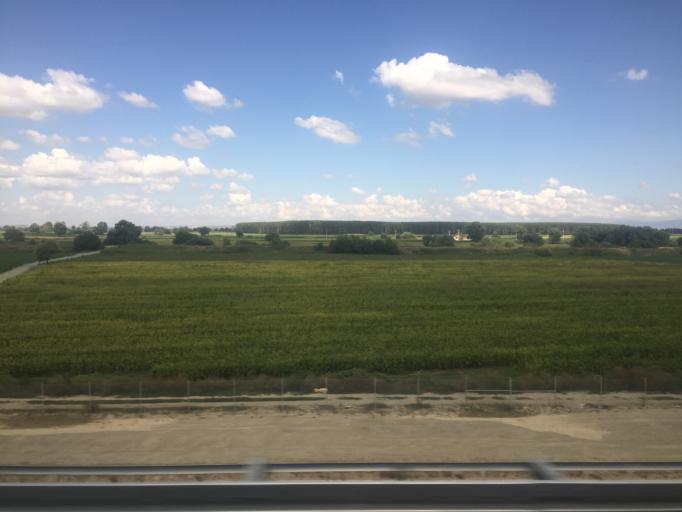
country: TR
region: Bursa
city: Tatkavakli
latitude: 40.0859
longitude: 28.2653
